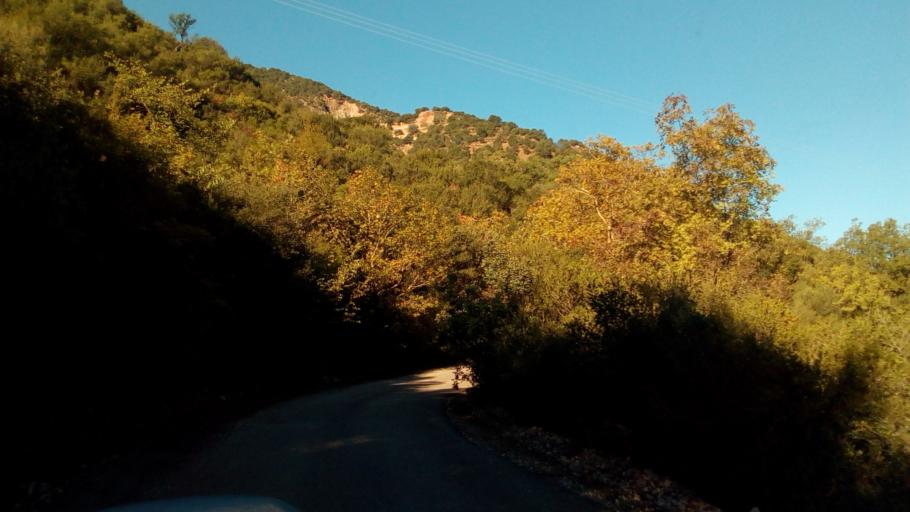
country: GR
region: West Greece
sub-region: Nomos Aitolias kai Akarnanias
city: Nafpaktos
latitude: 38.4659
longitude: 21.8720
